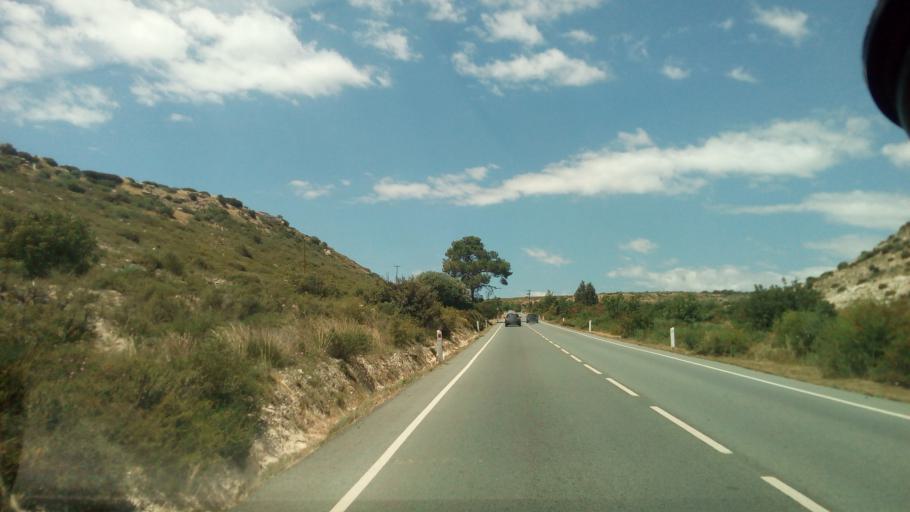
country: CY
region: Limassol
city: Erimi
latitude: 34.7025
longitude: 32.8956
